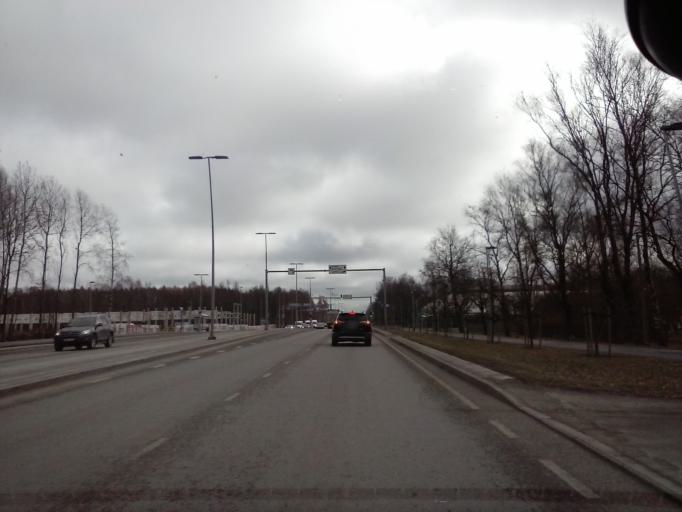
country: EE
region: Harju
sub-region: Saue vald
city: Laagri
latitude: 59.4222
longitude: 24.6481
